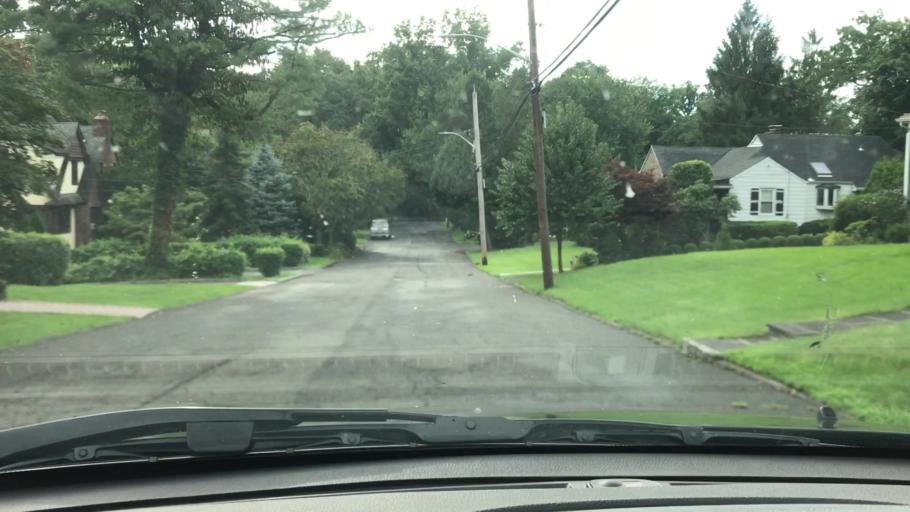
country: US
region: New York
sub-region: Westchester County
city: New Rochelle
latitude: 40.9353
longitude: -73.7960
